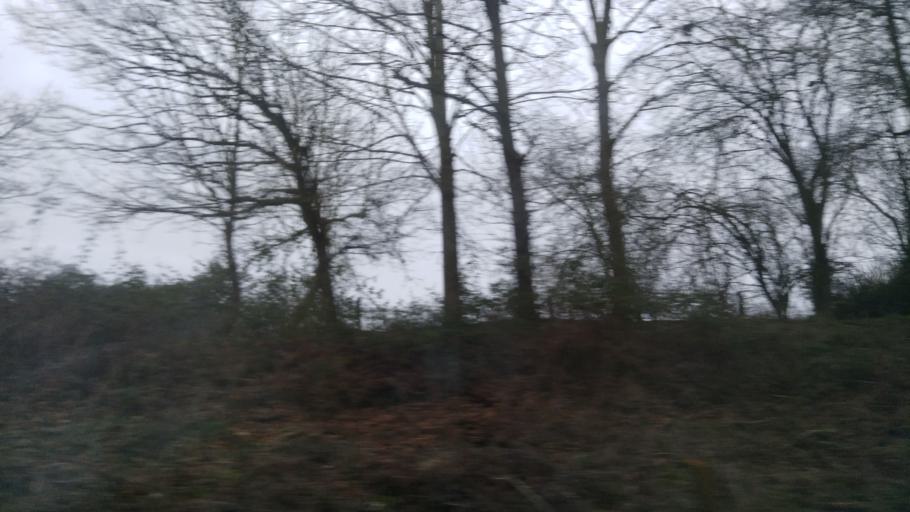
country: GB
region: England
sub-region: Kent
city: Marden
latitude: 51.1753
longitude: 0.4967
